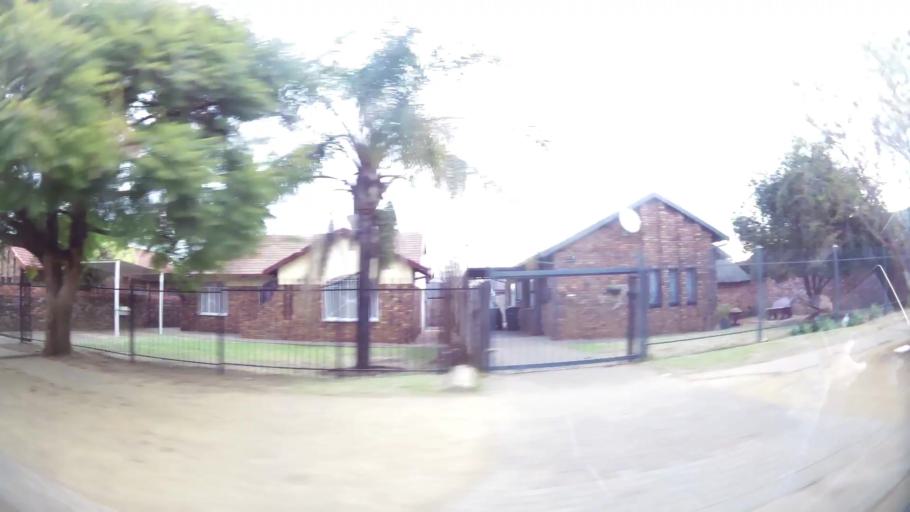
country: ZA
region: Gauteng
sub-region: City of Tshwane Metropolitan Municipality
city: Pretoria
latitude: -25.7037
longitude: 28.3050
